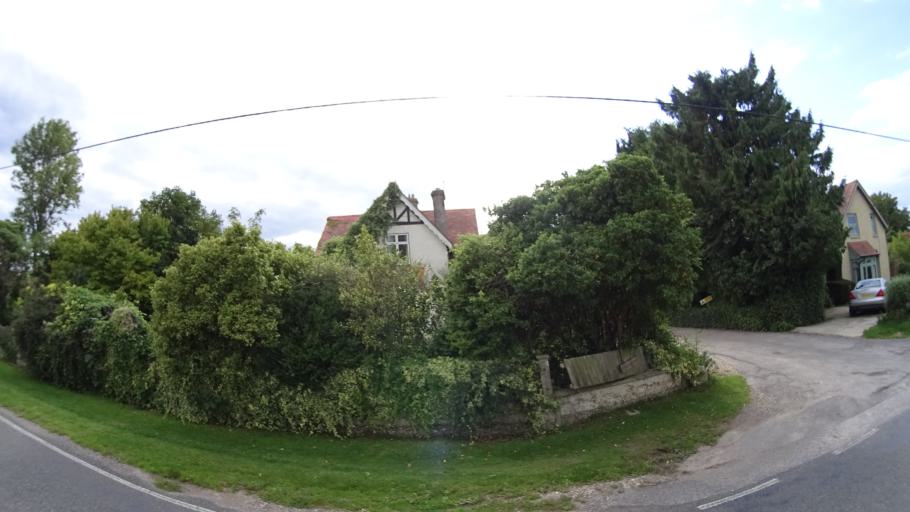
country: GB
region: England
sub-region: Hampshire
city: East Dean
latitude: 51.0984
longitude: -1.5697
